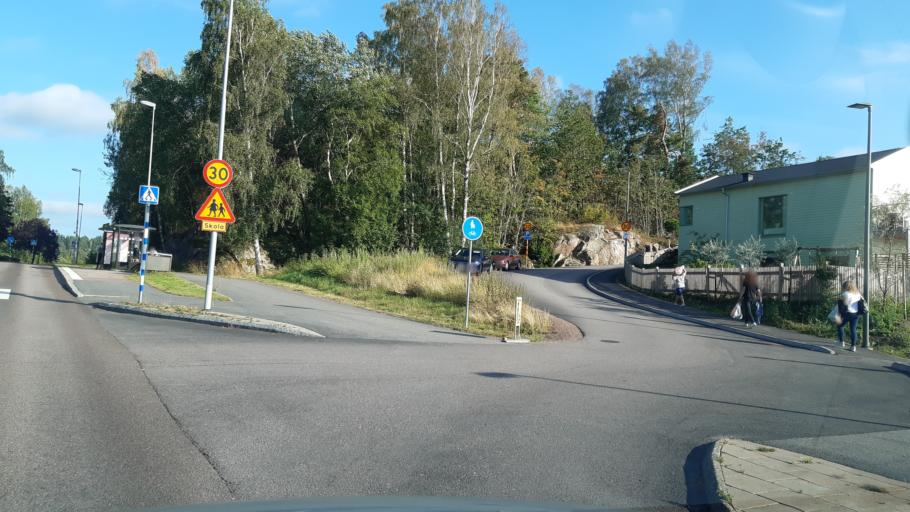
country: SE
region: Vaestra Goetaland
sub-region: Partille Kommun
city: Partille
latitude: 57.7179
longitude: 12.0700
